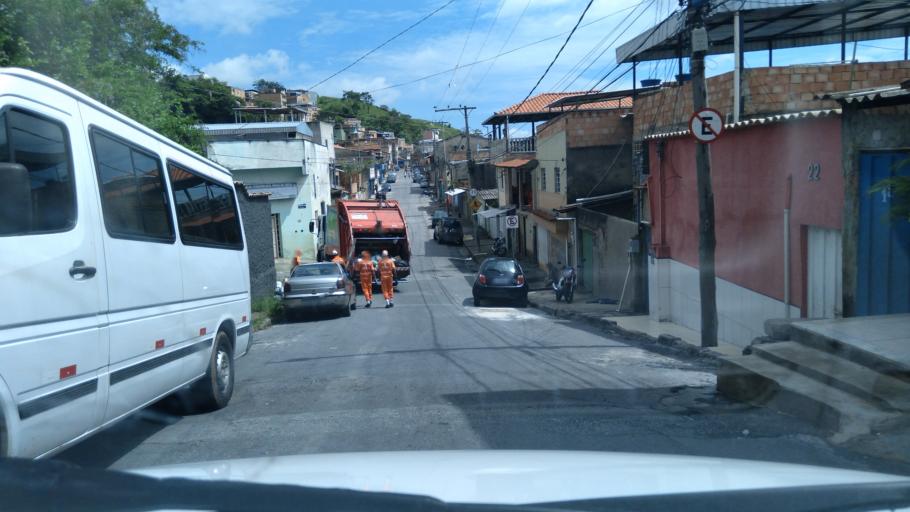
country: BR
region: Minas Gerais
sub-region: Belo Horizonte
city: Belo Horizonte
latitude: -19.8968
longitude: -43.8904
